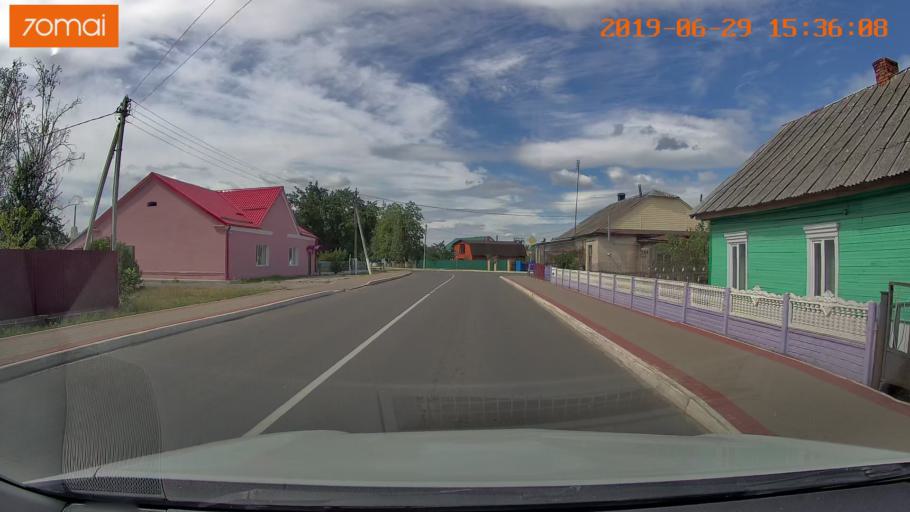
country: BY
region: Brest
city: Mikashevichy
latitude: 52.2190
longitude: 27.4699
